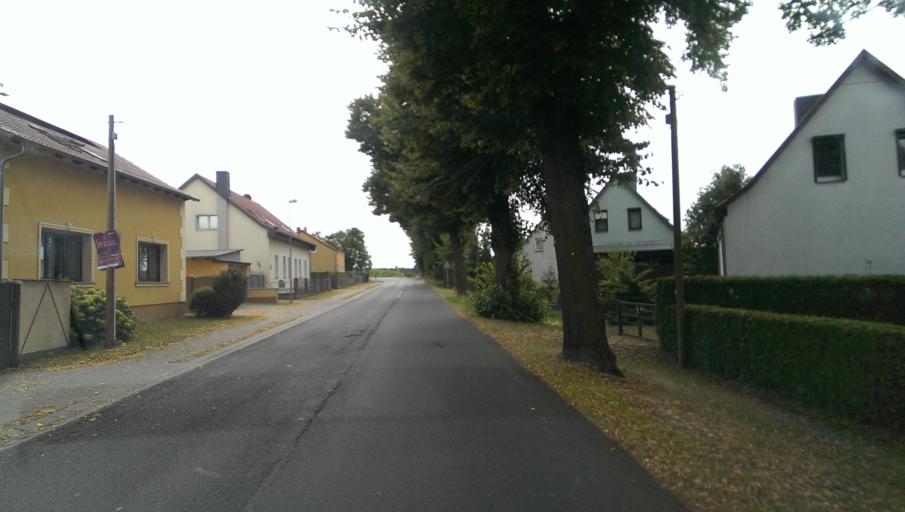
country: DE
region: Brandenburg
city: Trebbin
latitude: 52.1994
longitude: 13.2096
